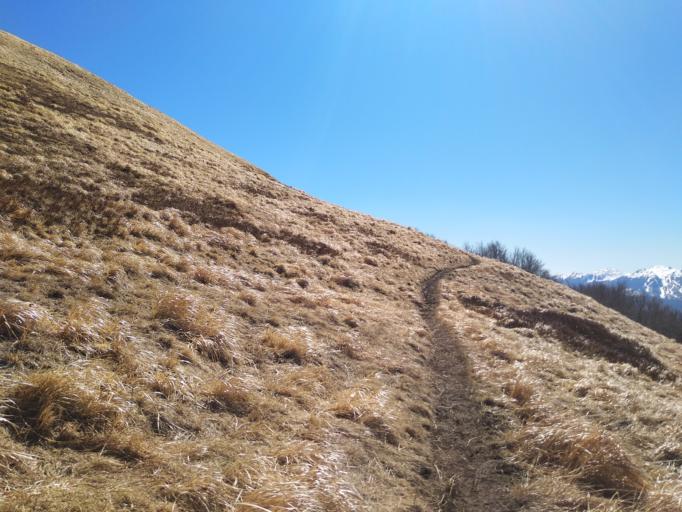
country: IT
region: Emilia-Romagna
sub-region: Provincia di Reggio Emilia
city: Collagna
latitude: 44.3749
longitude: 10.2846
